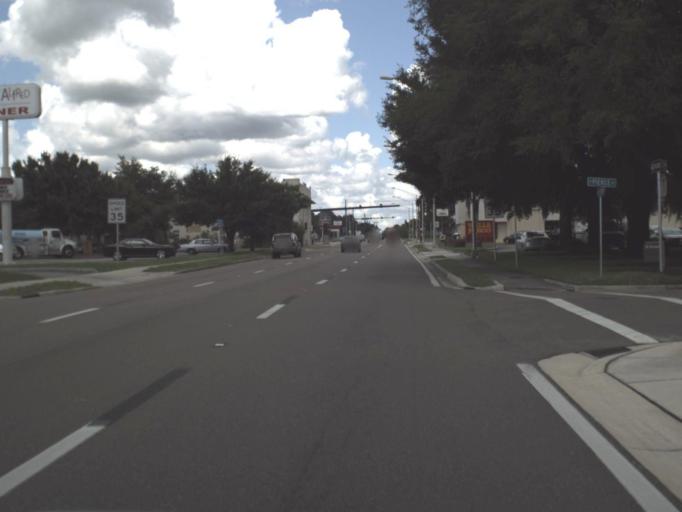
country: US
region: Florida
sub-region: Polk County
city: Lake Alfred
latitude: 28.0904
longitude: -81.7296
